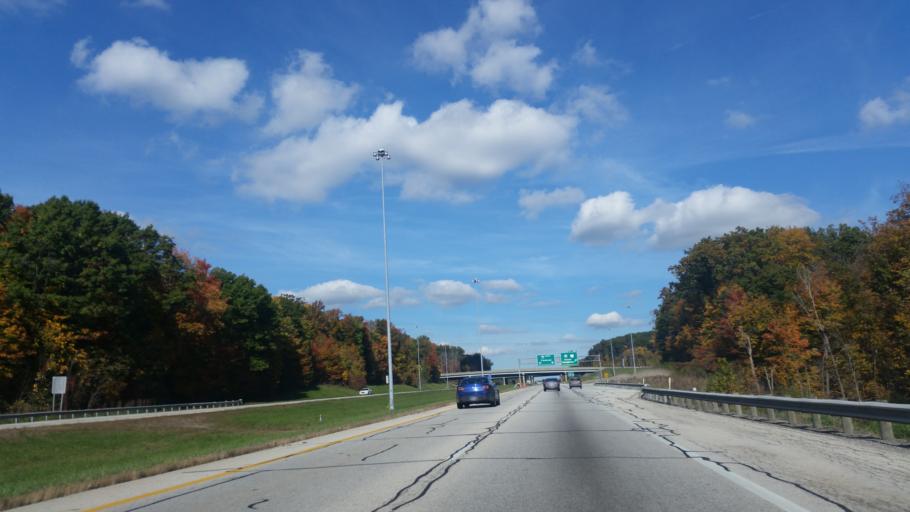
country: US
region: Ohio
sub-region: Summit County
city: Richfield
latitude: 41.2695
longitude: -81.6362
